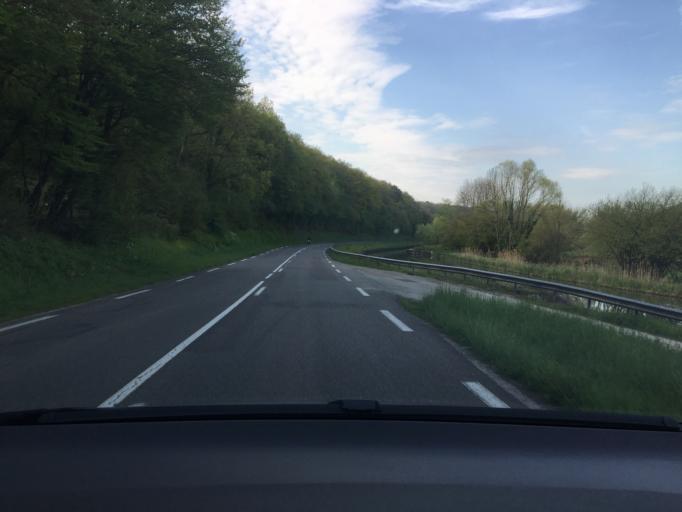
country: FR
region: Franche-Comte
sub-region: Departement du Doubs
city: Courcelles-les-Montbeliard
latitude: 47.4938
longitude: 6.7793
